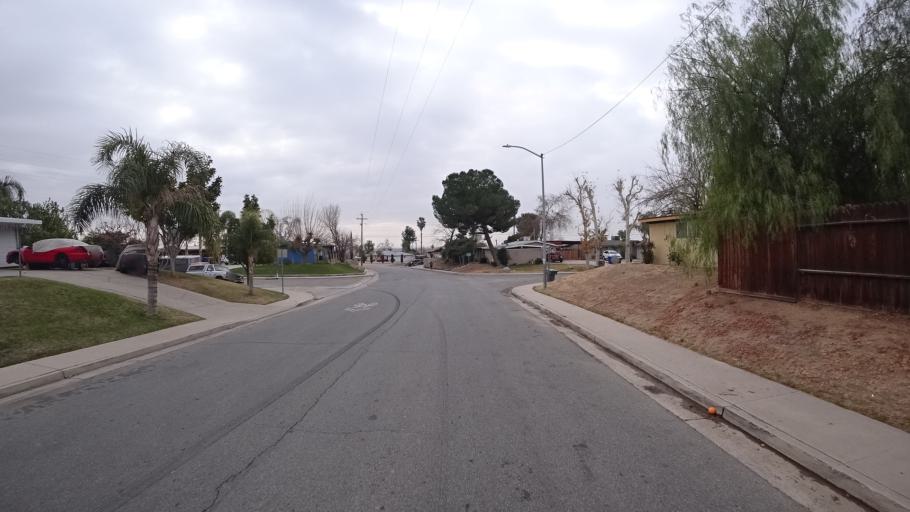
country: US
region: California
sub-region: Kern County
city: Bakersfield
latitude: 35.3805
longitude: -118.9256
